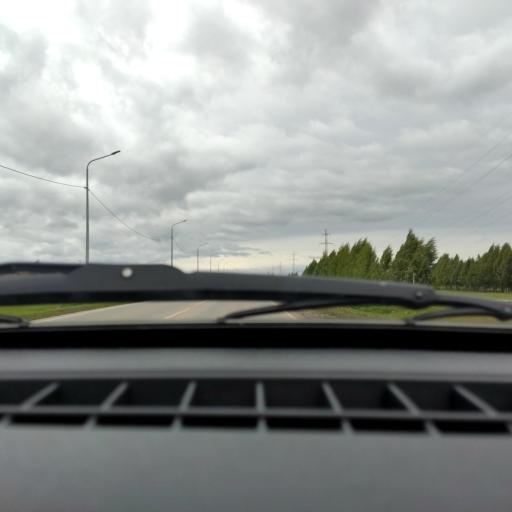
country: RU
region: Bashkortostan
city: Rayevskiy
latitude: 54.0609
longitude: 54.9124
